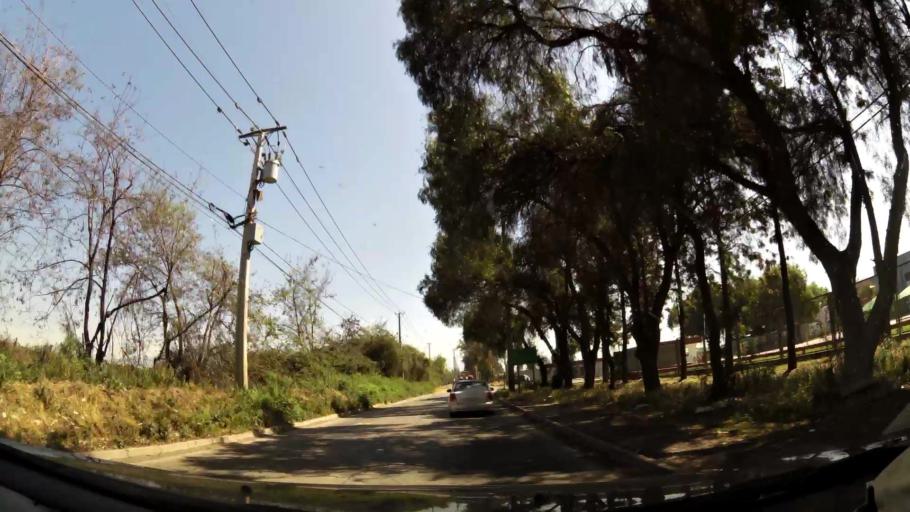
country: CL
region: Santiago Metropolitan
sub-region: Provincia de Santiago
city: Lo Prado
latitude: -33.3936
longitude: -70.7714
